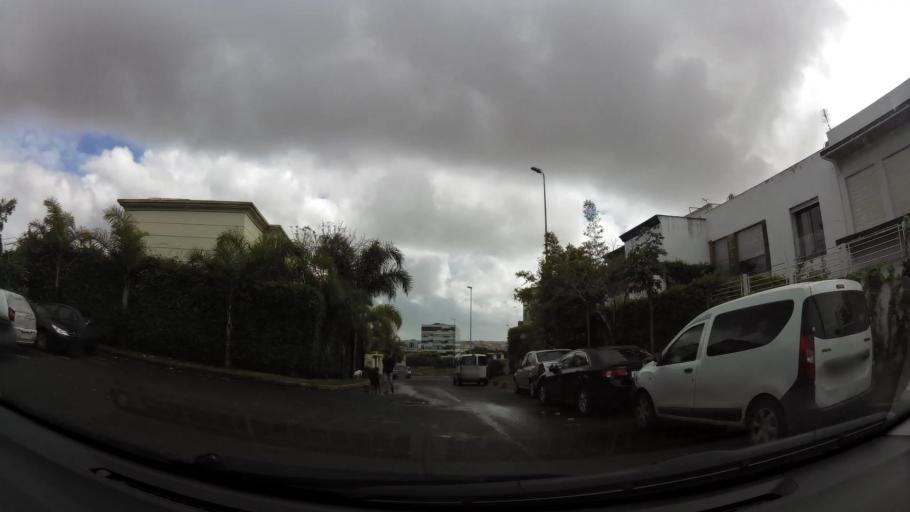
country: MA
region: Grand Casablanca
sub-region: Casablanca
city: Casablanca
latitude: 33.5289
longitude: -7.6419
